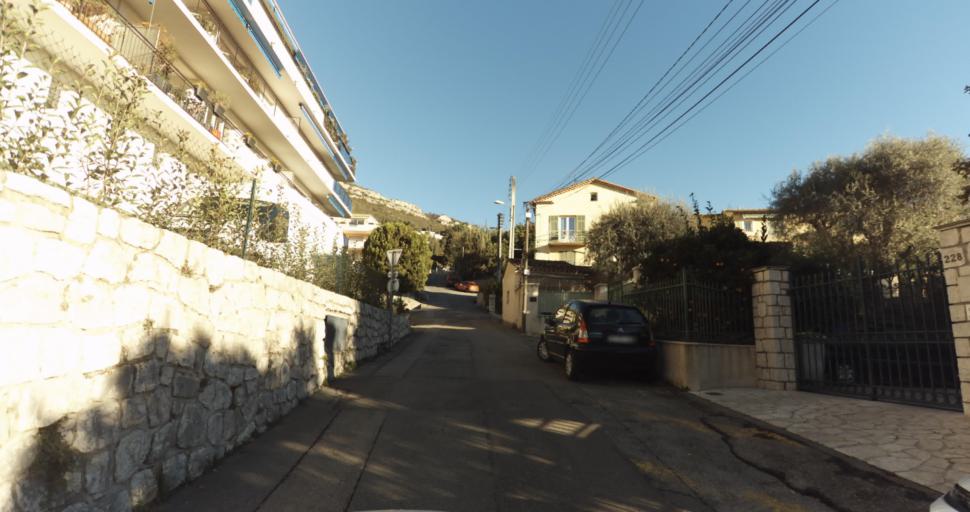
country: FR
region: Provence-Alpes-Cote d'Azur
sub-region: Departement des Alpes-Maritimes
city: Vence
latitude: 43.7255
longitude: 7.1139
